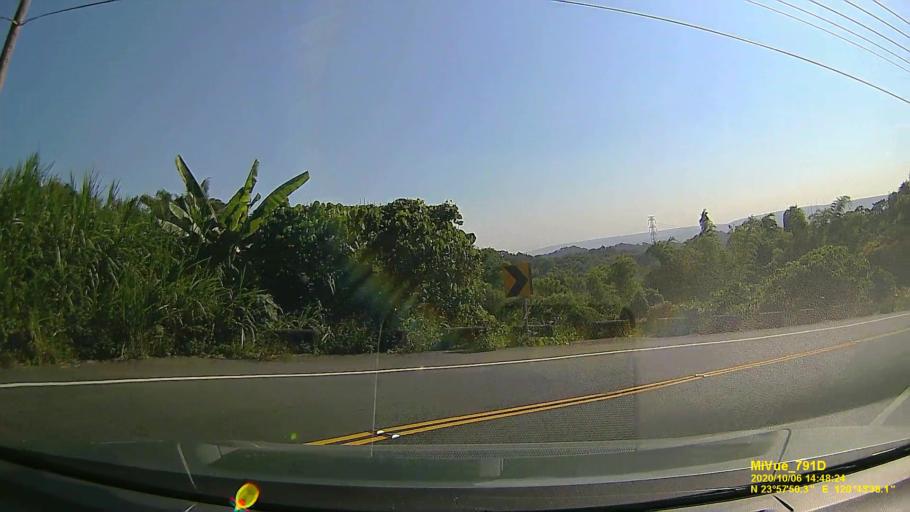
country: TW
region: Taiwan
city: Zhongxing New Village
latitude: 23.9640
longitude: 120.7273
